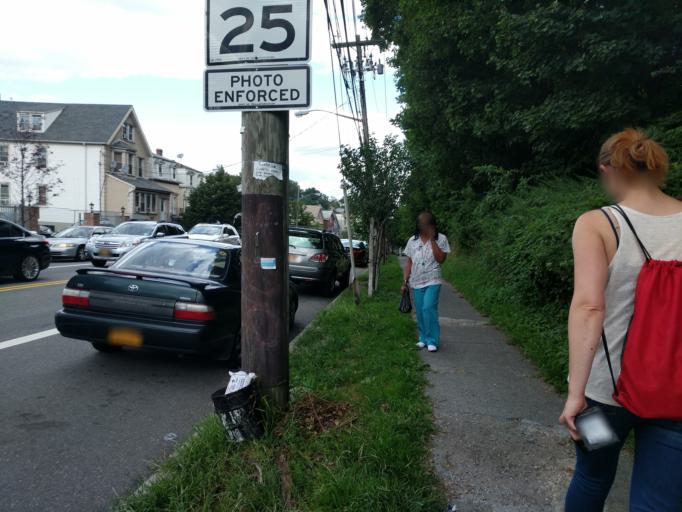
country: US
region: New Jersey
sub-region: Hudson County
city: Bayonne
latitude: 40.6343
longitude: -74.0854
